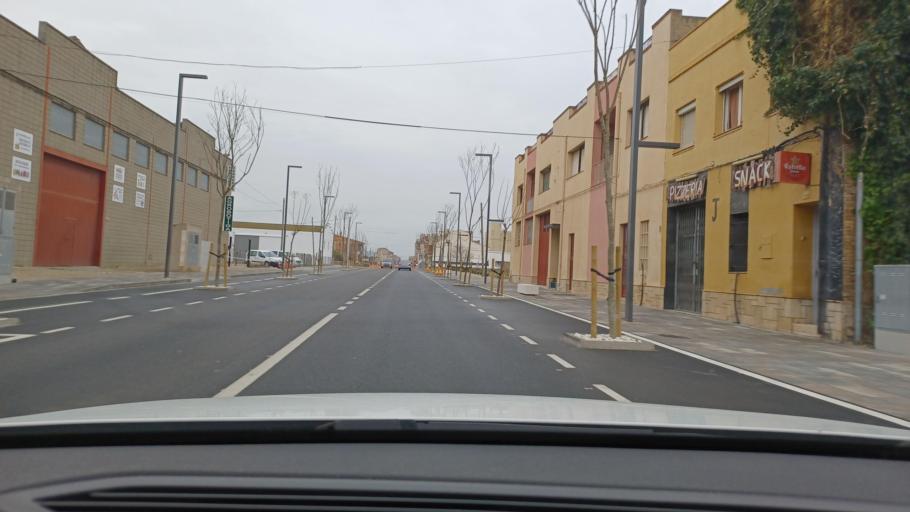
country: ES
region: Catalonia
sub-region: Provincia de Tarragona
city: Amposta
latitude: 40.7456
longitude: 0.6187
